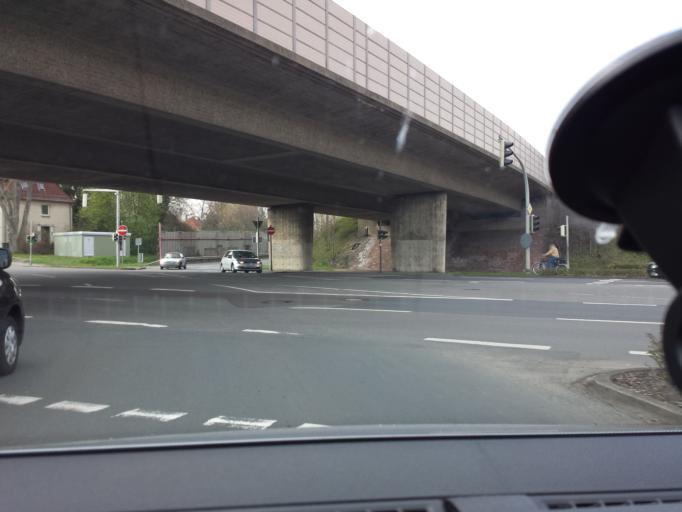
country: DE
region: Lower Saxony
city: Braunschweig
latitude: 52.2721
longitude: 10.4928
